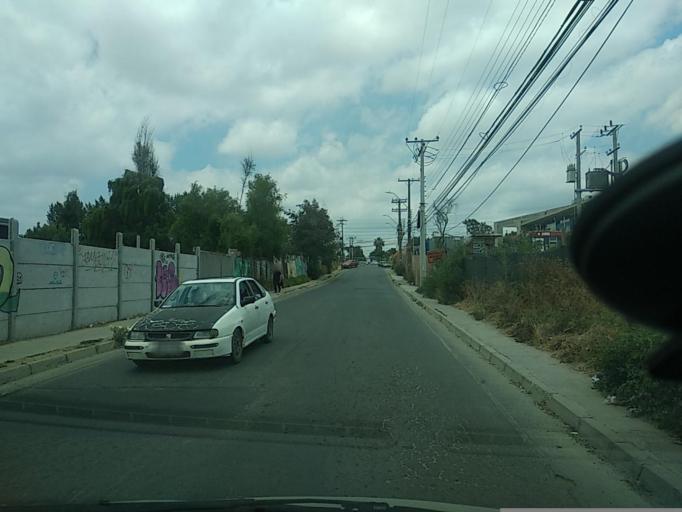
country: CL
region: Valparaiso
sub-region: Provincia de Marga Marga
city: Villa Alemana
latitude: -33.0415
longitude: -71.4076
